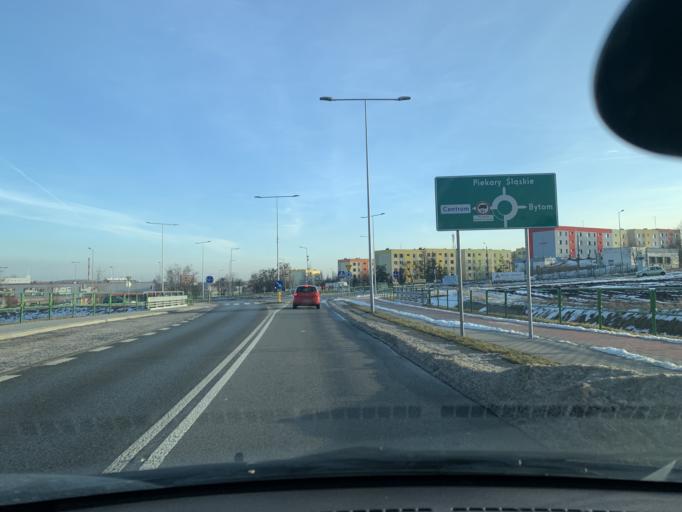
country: PL
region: Silesian Voivodeship
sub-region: Powiat tarnogorski
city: Radzionkow
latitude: 50.4003
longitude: 18.8913
